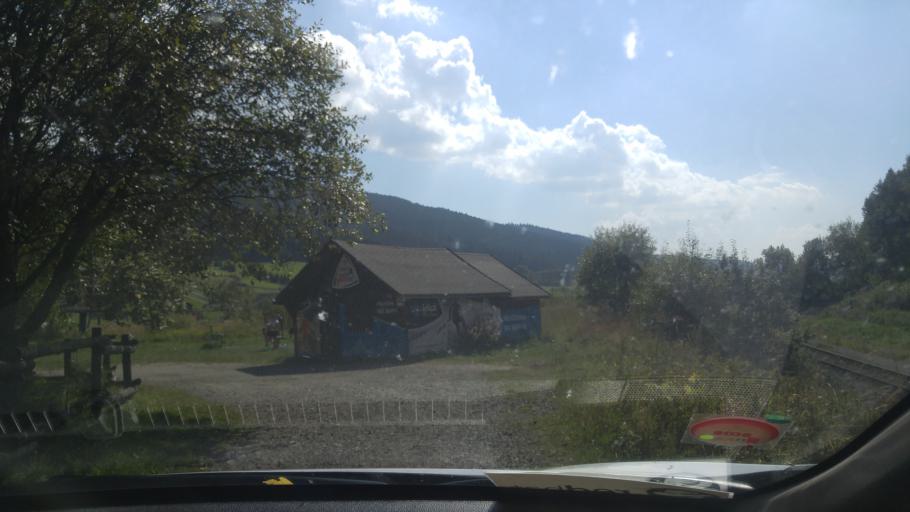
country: CZ
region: Olomoucky
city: Vapenna
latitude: 50.1933
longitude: 17.0638
